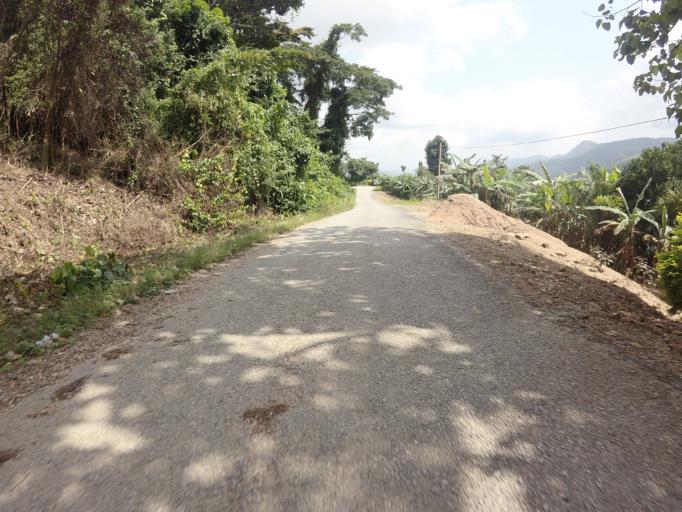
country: GH
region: Volta
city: Kpandu
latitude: 6.8273
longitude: 0.4250
